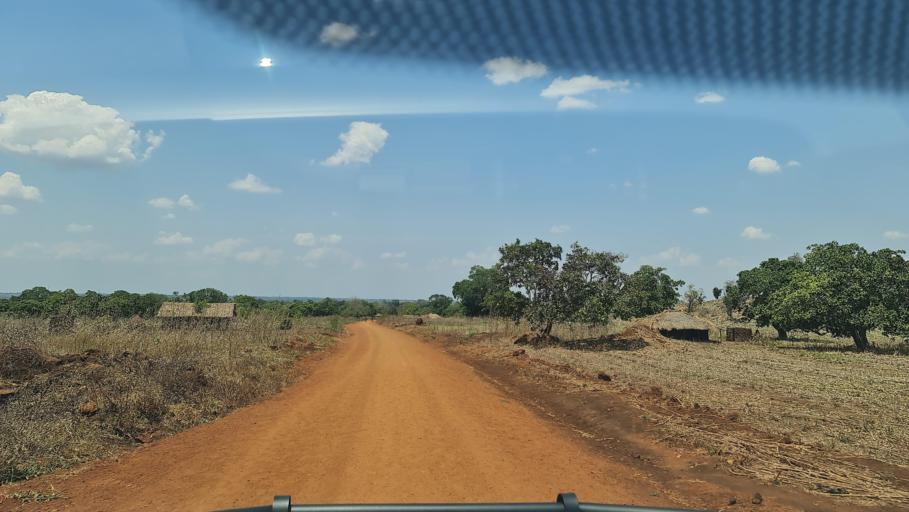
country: MZ
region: Nampula
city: Nacala
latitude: -14.7983
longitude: 40.0700
